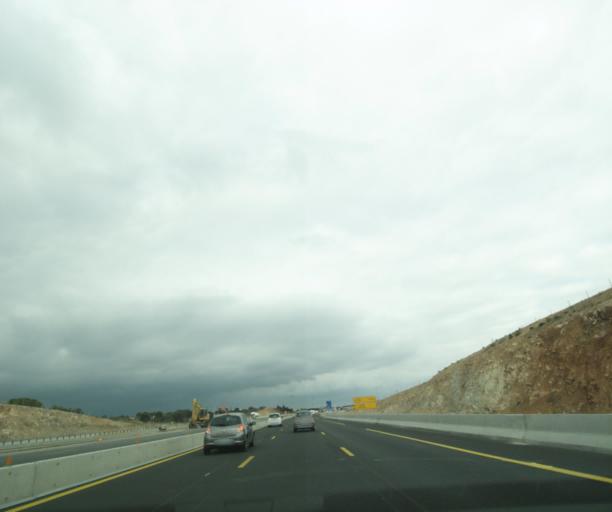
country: FR
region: Languedoc-Roussillon
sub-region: Departement de l'Herault
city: Saint-Jean-de-Vedas
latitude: 43.5573
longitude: 3.8251
